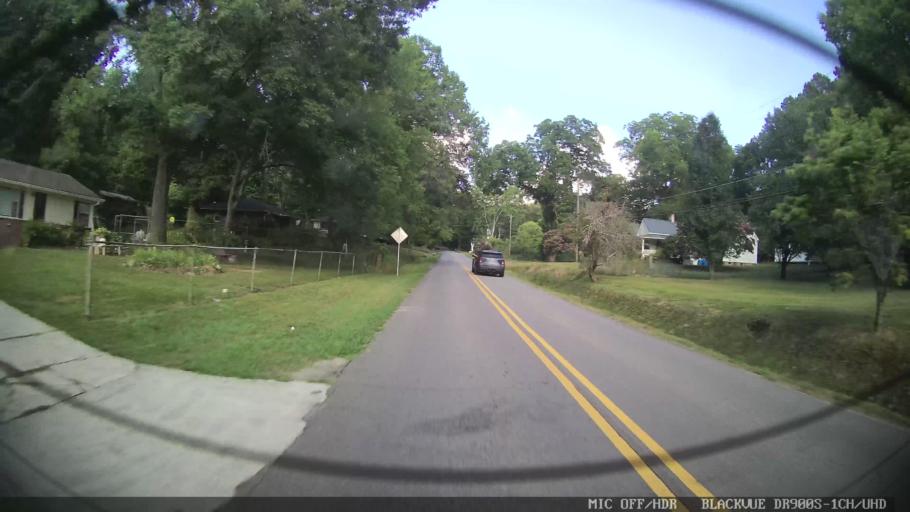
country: US
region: Georgia
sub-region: Floyd County
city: Rome
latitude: 34.2333
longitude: -85.1567
